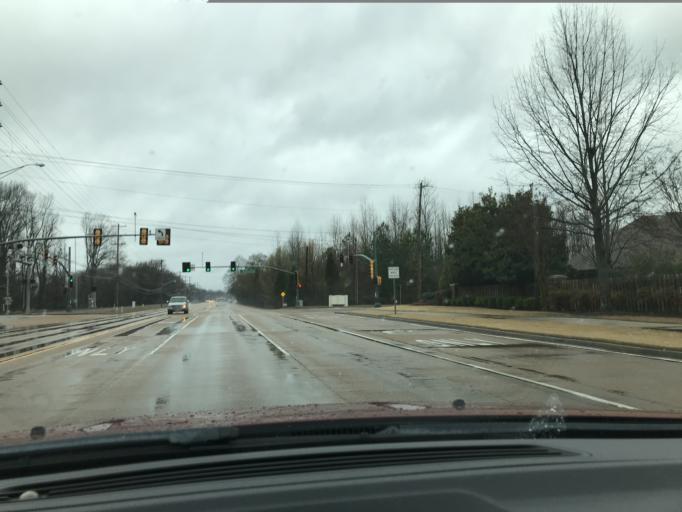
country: US
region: Tennessee
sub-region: Shelby County
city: Collierville
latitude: 35.0489
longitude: -89.7234
